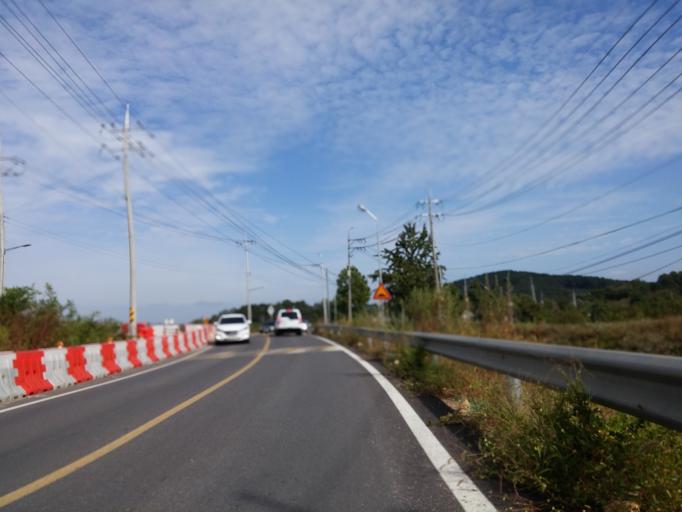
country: KR
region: Chungcheongnam-do
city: Yonmu
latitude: 36.1758
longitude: 127.1430
